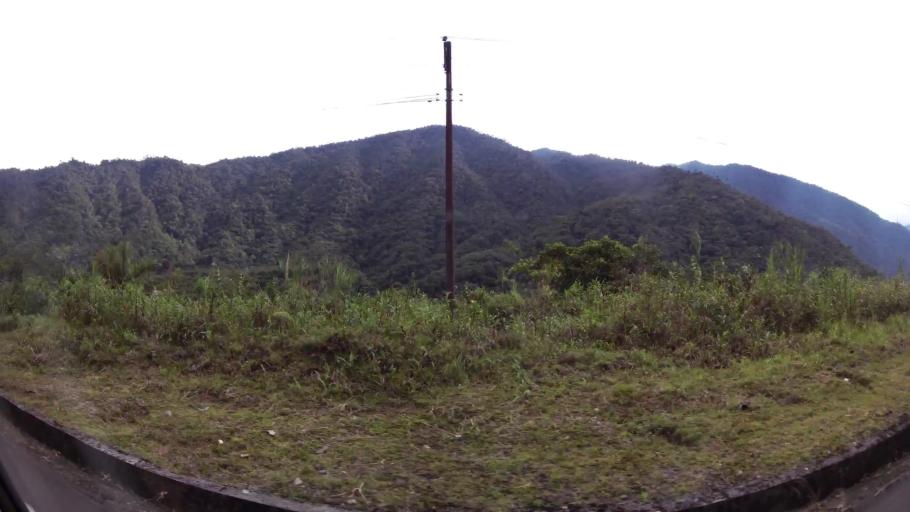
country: EC
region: Pastaza
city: Puyo
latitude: -1.4500
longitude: -78.1563
